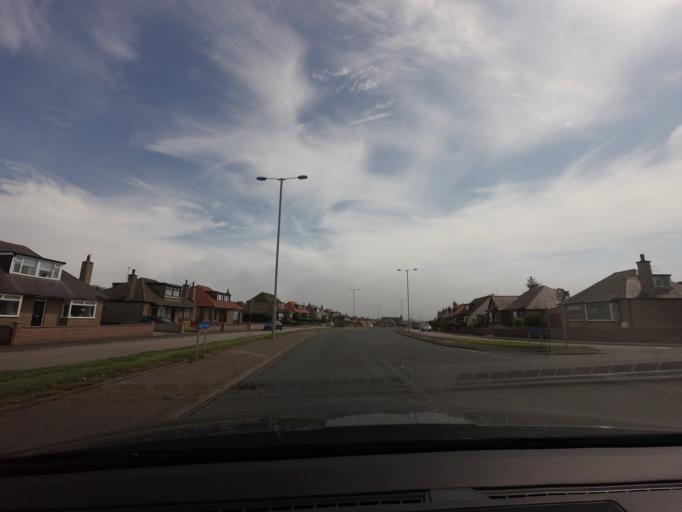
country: GB
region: Scotland
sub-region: Aberdeenshire
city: Peterhead
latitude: 57.5072
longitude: -1.8033
